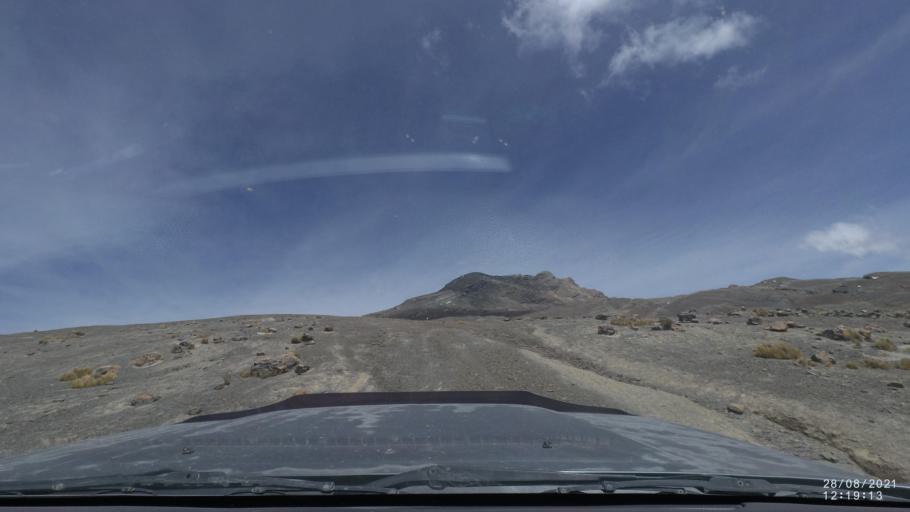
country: BO
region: Cochabamba
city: Sipe Sipe
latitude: -17.2802
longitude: -66.3826
